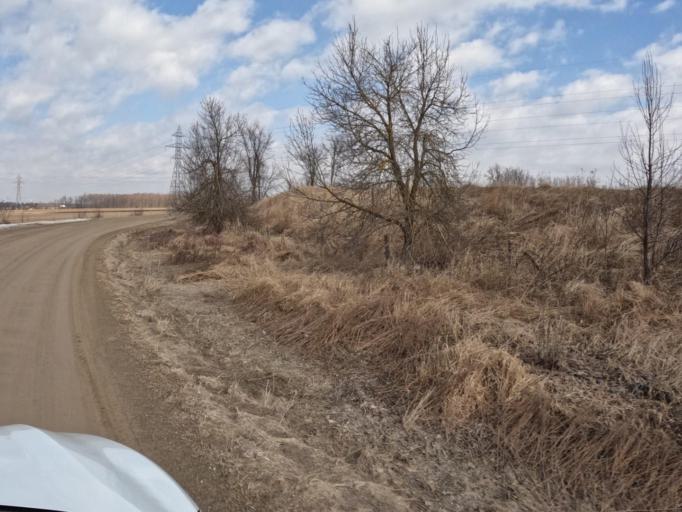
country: CA
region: Ontario
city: Shelburne
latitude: 43.9419
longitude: -80.2461
